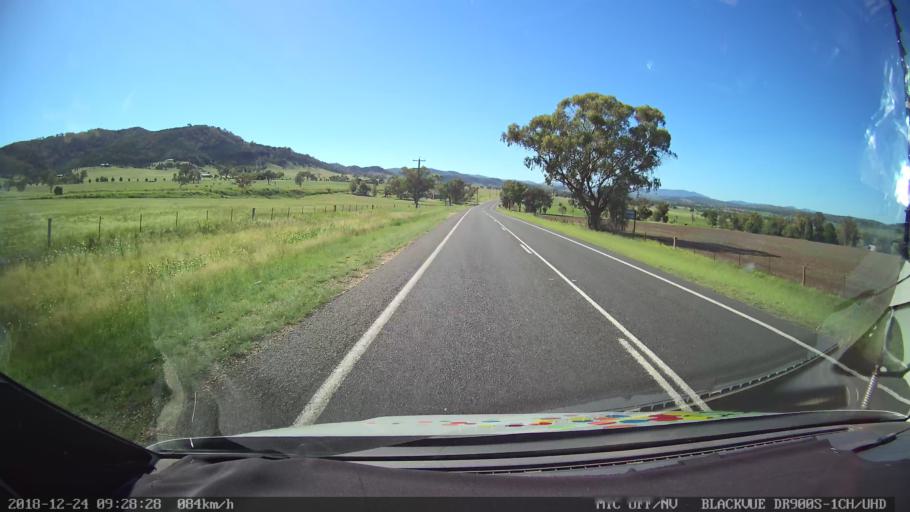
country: AU
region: New South Wales
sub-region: Liverpool Plains
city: Quirindi
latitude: -31.5382
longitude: 150.6890
